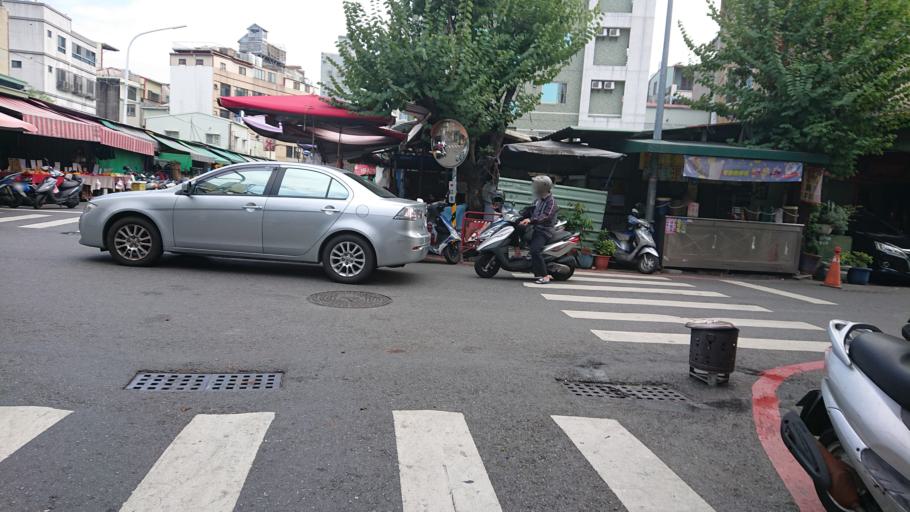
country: TW
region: Taiwan
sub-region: Tainan
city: Tainan
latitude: 22.9998
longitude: 120.2036
